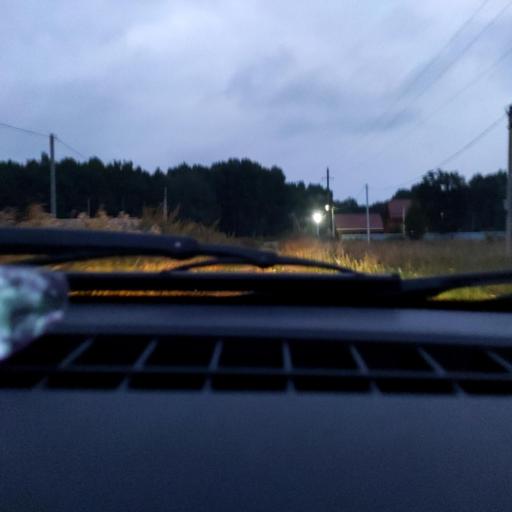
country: RU
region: Bashkortostan
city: Iglino
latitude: 54.7304
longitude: 56.3286
